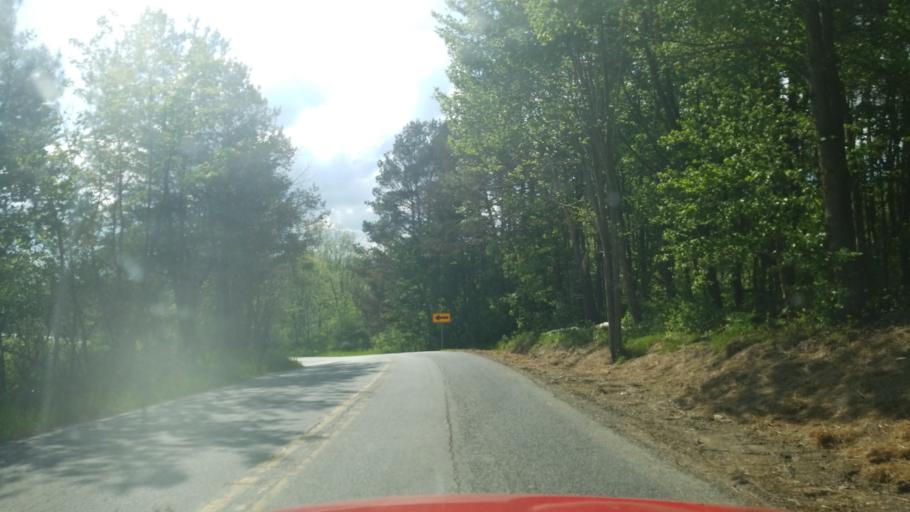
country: US
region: Pennsylvania
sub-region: Clearfield County
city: Hyde
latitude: 40.9781
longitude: -78.4705
